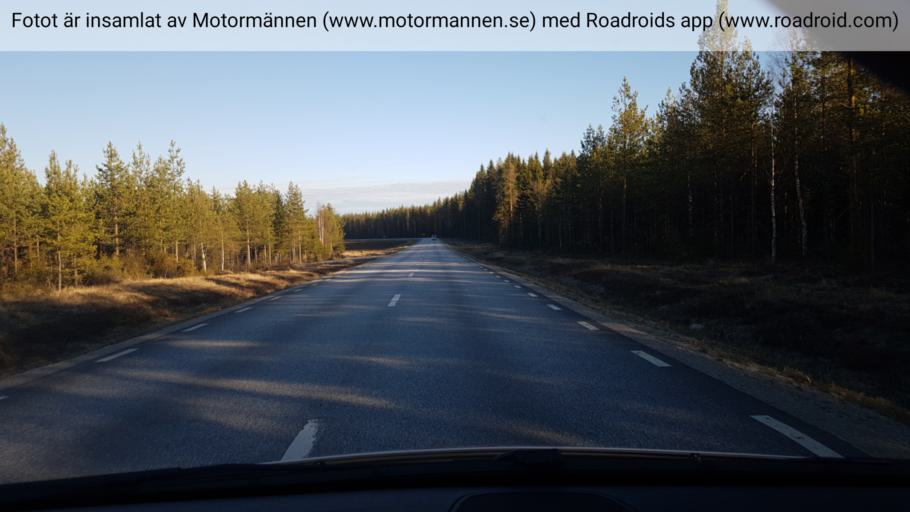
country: SE
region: Vaesterbotten
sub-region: Vindelns Kommun
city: Vindeln
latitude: 64.0955
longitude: 19.6078
